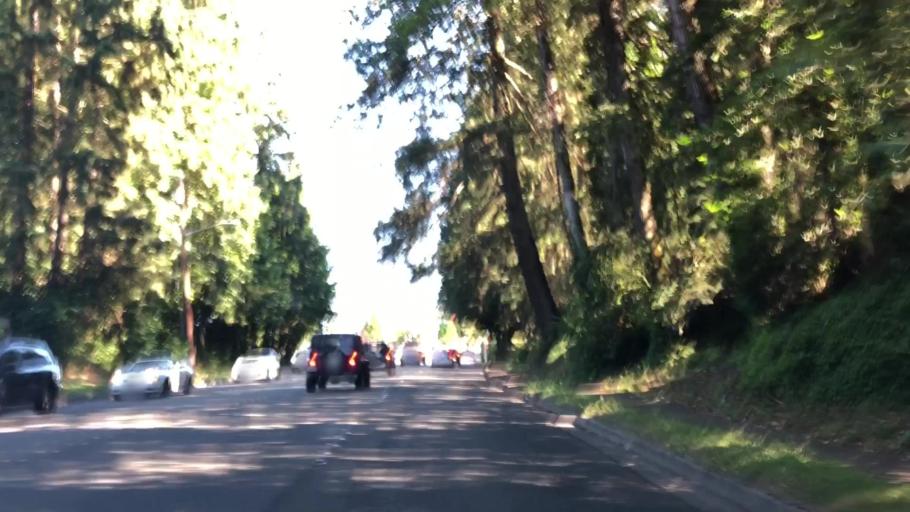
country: US
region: Washington
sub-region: King County
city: Redmond
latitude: 47.6470
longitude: -122.1150
